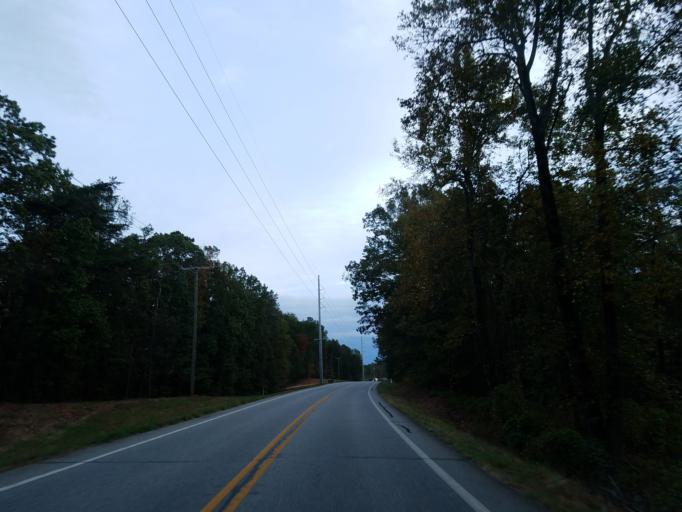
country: US
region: Georgia
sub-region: Dawson County
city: Dawsonville
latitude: 34.4627
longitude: -84.1747
